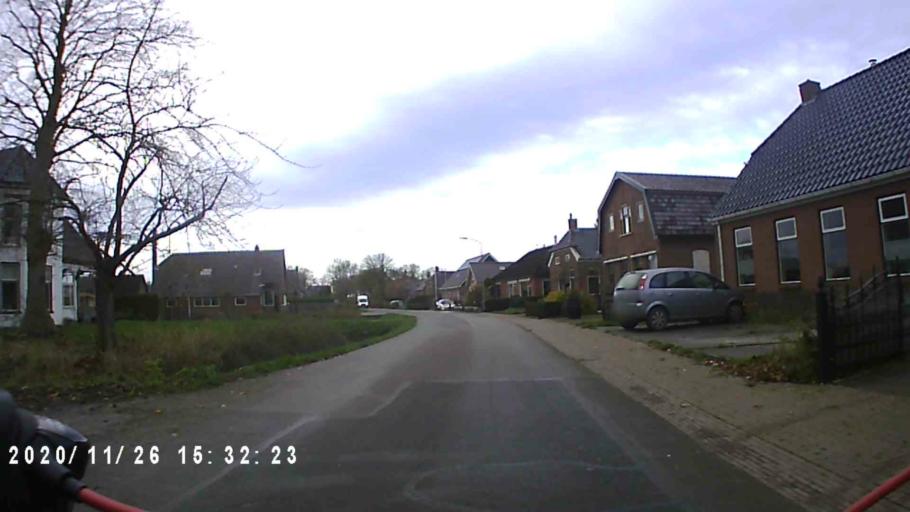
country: NL
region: Groningen
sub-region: Gemeente Slochteren
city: Slochteren
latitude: 53.3102
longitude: 6.7475
